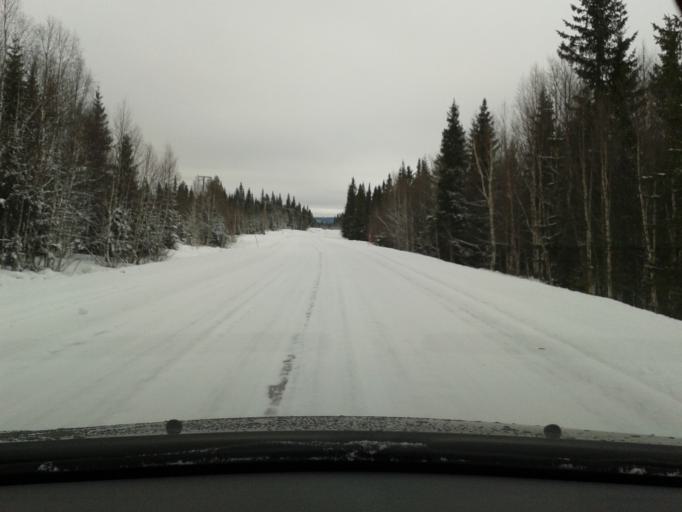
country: SE
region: Vaesterbotten
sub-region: Vilhelmina Kommun
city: Sjoberg
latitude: 65.2251
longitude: 15.9302
